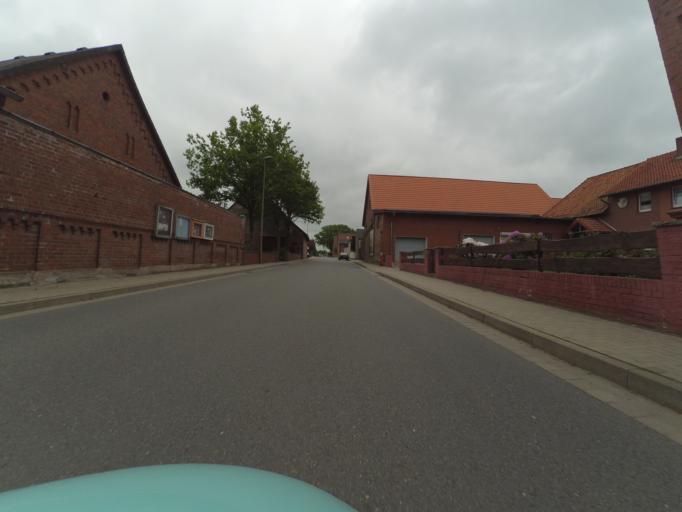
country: DE
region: Lower Saxony
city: Wendeburg
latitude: 52.3602
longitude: 10.3649
